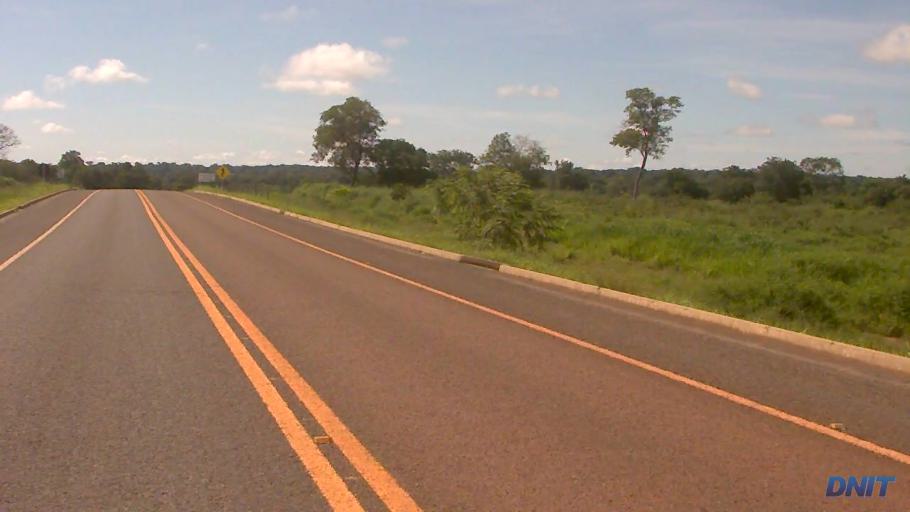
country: BR
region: Goias
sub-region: Sao Miguel Do Araguaia
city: Sao Miguel do Araguaia
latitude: -13.2866
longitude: -50.1814
